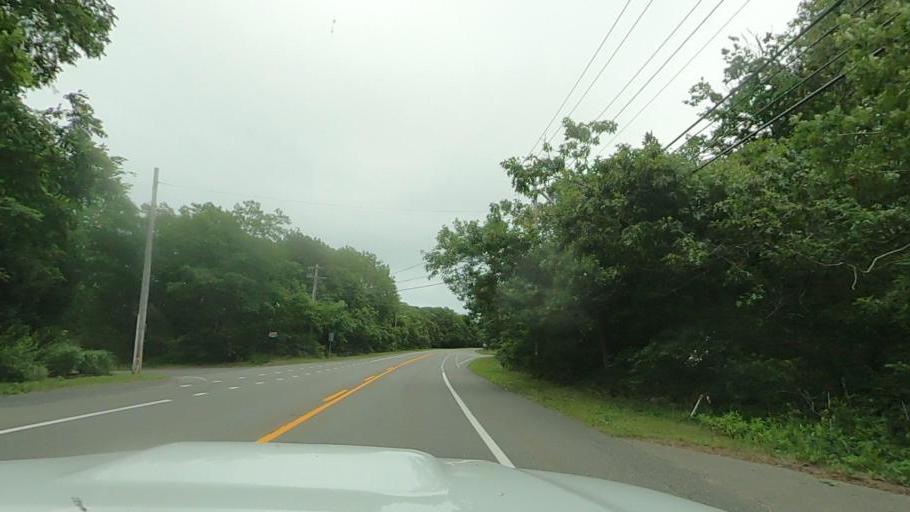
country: US
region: Massachusetts
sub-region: Barnstable County
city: Truro
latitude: 42.0039
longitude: -70.0545
